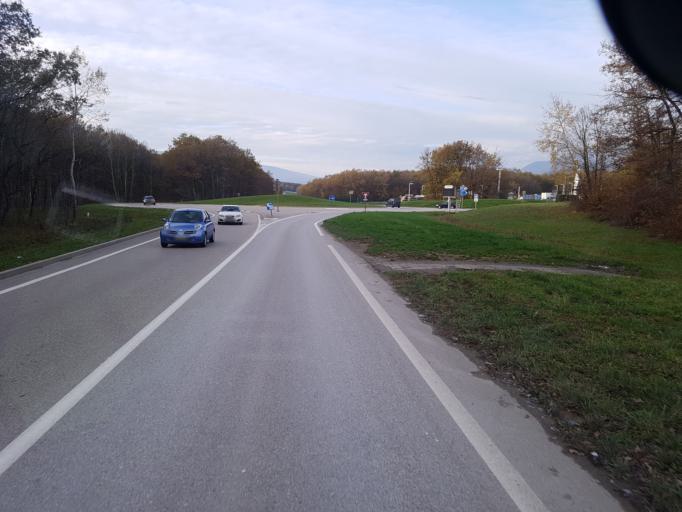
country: FR
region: Rhone-Alpes
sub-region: Departement de l'Ain
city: Bellegarde-sur-Valserine
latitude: 46.0636
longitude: 5.8629
